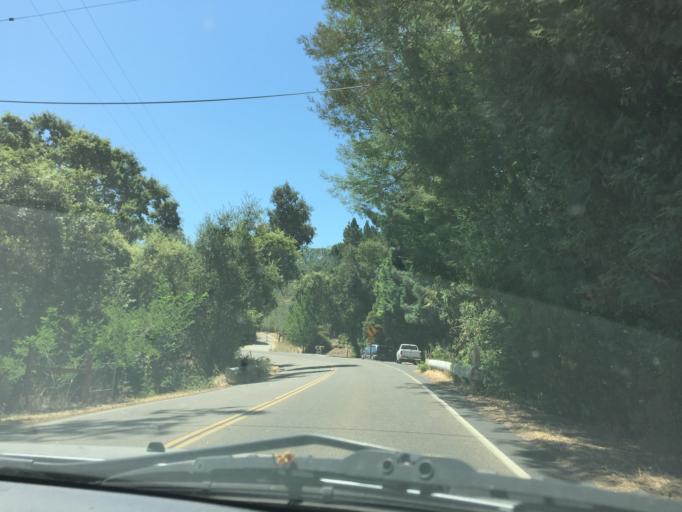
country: US
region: California
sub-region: Napa County
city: Napa
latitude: 38.2815
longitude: -122.3253
